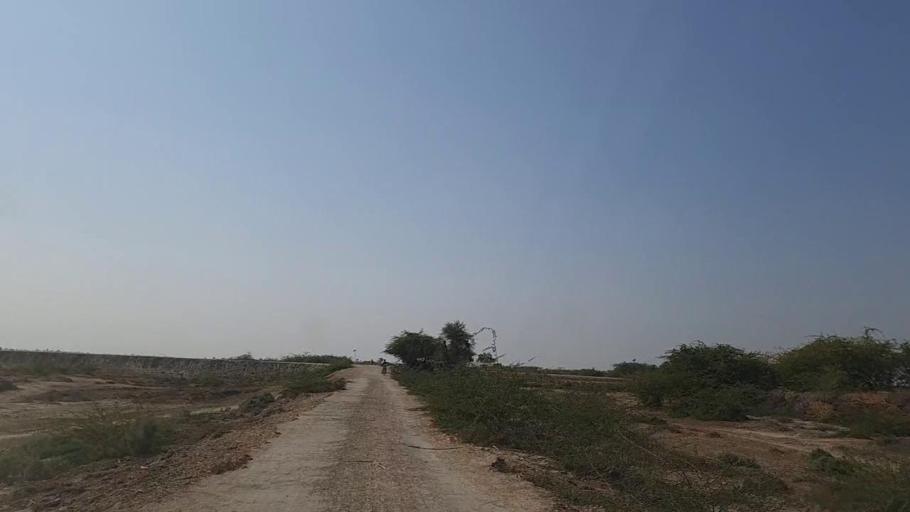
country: PK
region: Sindh
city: Naukot
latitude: 24.9023
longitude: 69.4345
